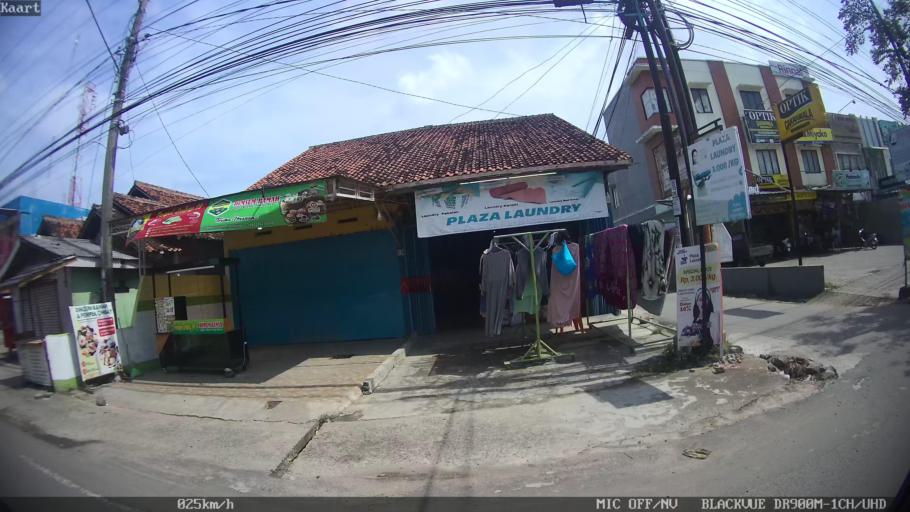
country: ID
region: Lampung
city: Kedaton
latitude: -5.3624
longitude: 105.2795
